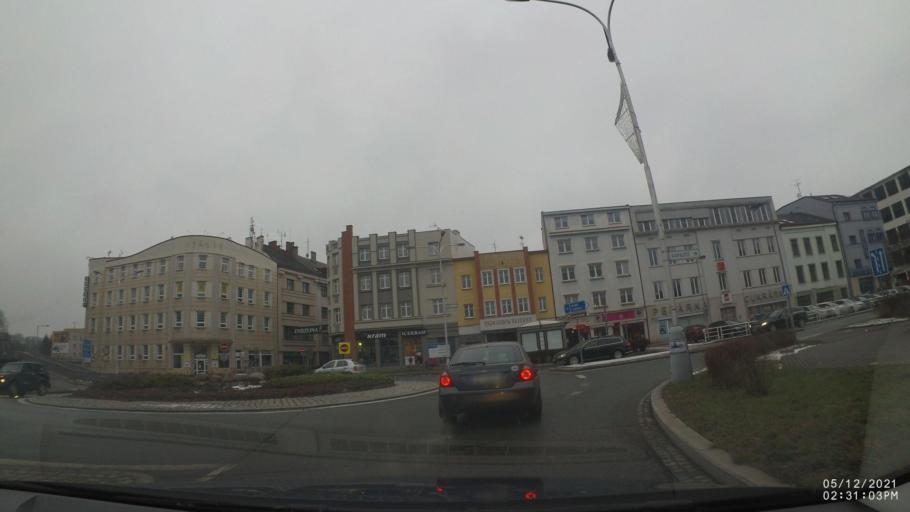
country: CZ
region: Kralovehradecky
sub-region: Okres Nachod
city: Nachod
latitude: 50.4175
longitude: 16.1692
